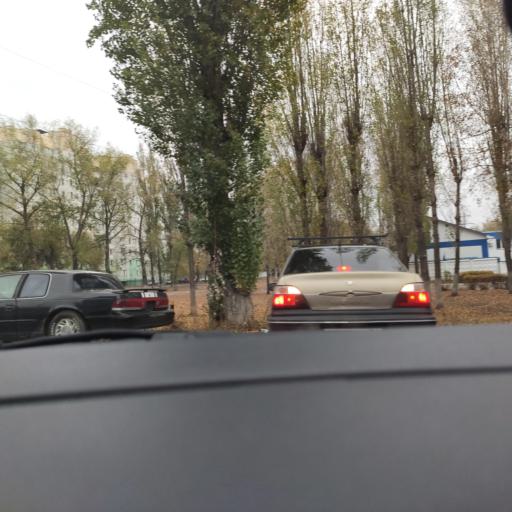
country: RU
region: Voronezj
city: Podgornoye
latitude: 51.6964
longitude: 39.1429
